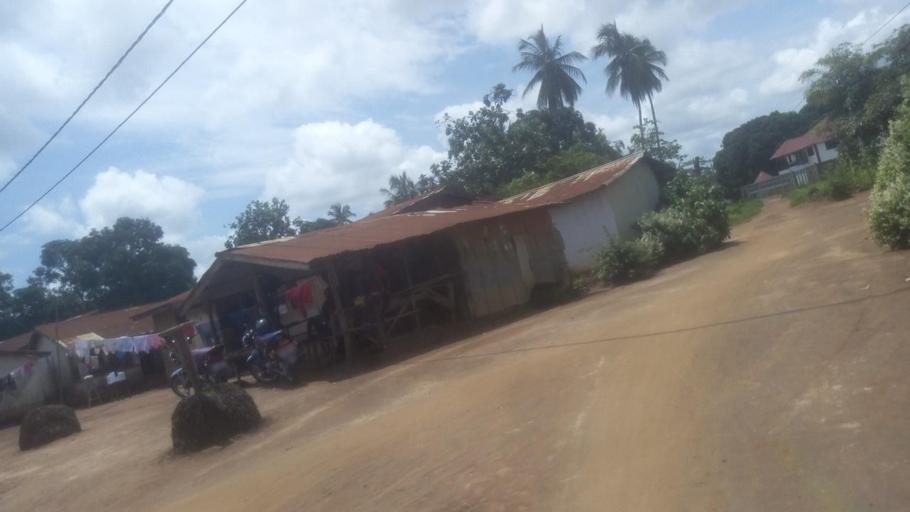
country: SL
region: Northern Province
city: Masoyila
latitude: 8.6070
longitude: -13.1968
